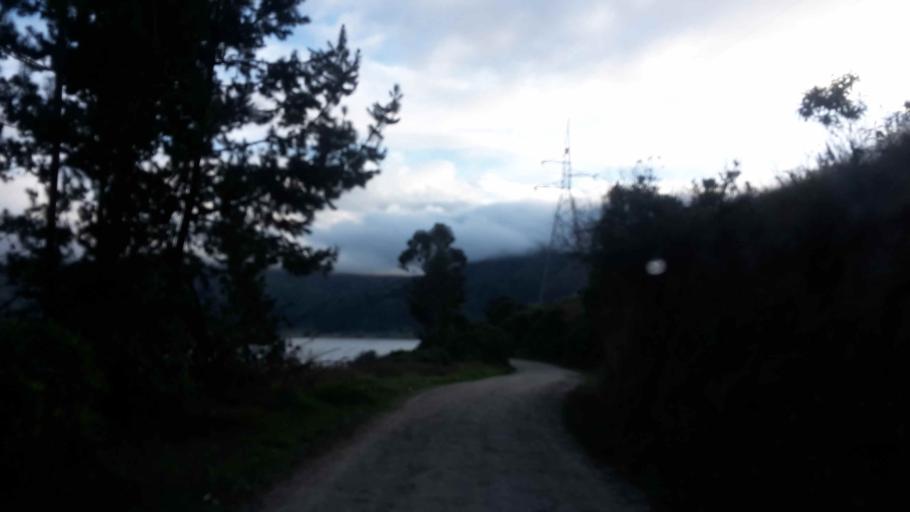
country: BO
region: Cochabamba
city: Colomi
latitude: -17.2744
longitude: -65.9072
